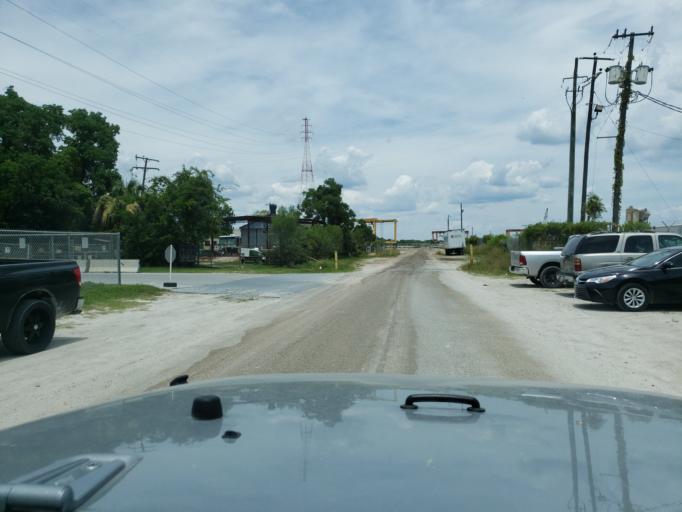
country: US
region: Georgia
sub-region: Chatham County
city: Thunderbolt
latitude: 32.0751
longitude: -81.0521
